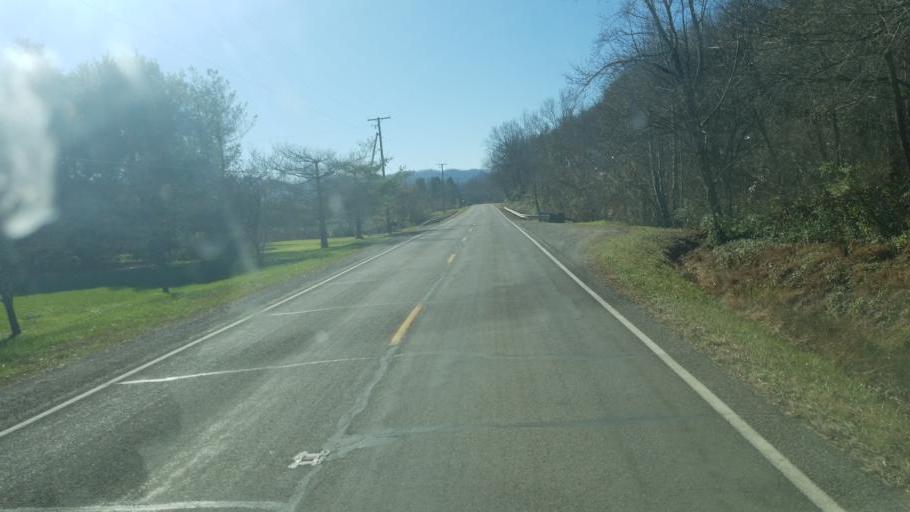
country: US
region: Kentucky
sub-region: Lewis County
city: Vanceburg
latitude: 38.6218
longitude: -83.2669
